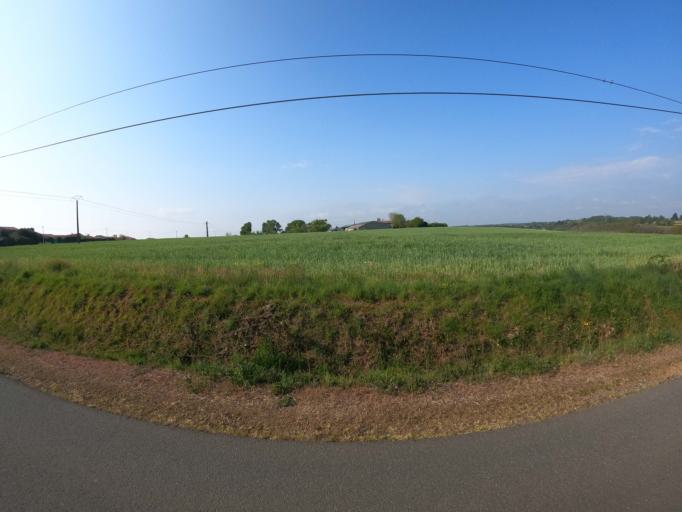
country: FR
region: Pays de la Loire
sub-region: Departement de Maine-et-Loire
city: La Seguiniere
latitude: 47.0673
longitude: -0.9550
